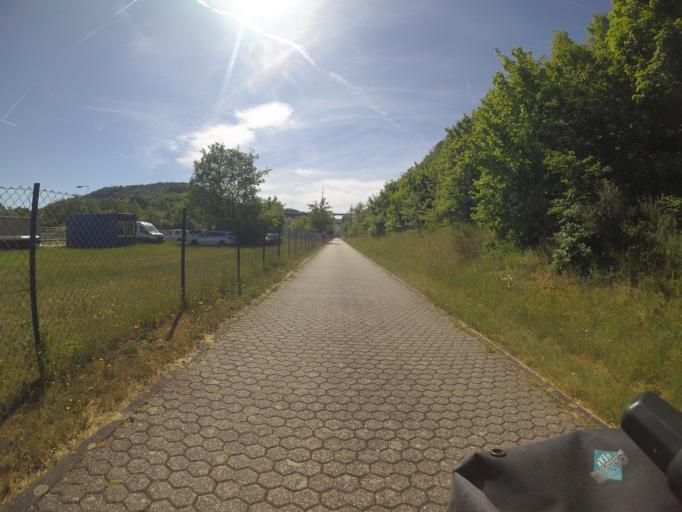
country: DE
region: Rheinland-Pfalz
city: Kanzem
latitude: 49.6585
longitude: 6.5599
